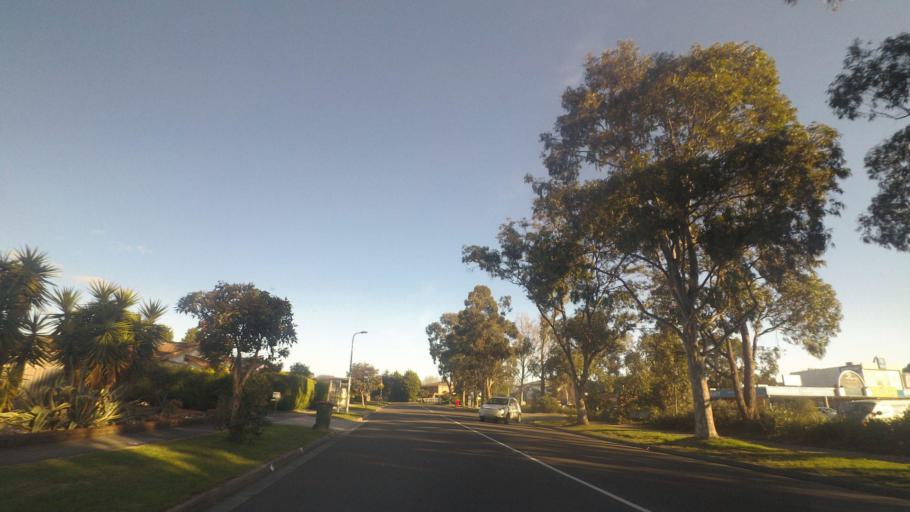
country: AU
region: Victoria
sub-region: Knox
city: Knoxfield
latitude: -37.9136
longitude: 145.2579
